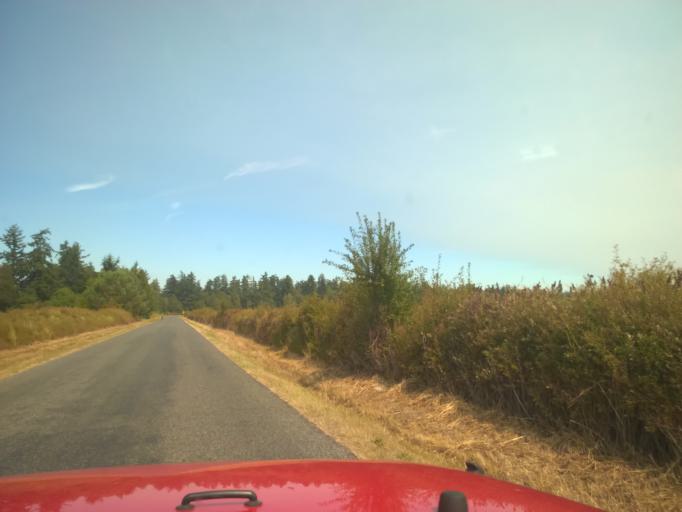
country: US
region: Washington
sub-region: San Juan County
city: Friday Harbor
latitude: 48.5214
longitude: -122.8827
